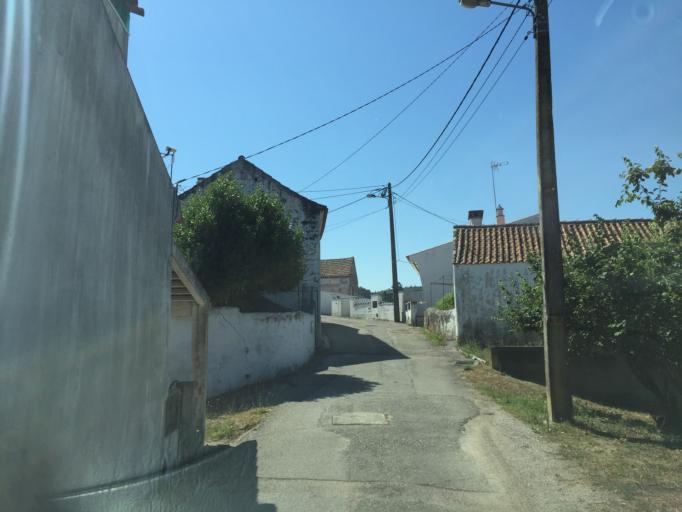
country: PT
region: Santarem
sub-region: Constancia
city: Constancia
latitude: 39.5452
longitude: -8.2747
